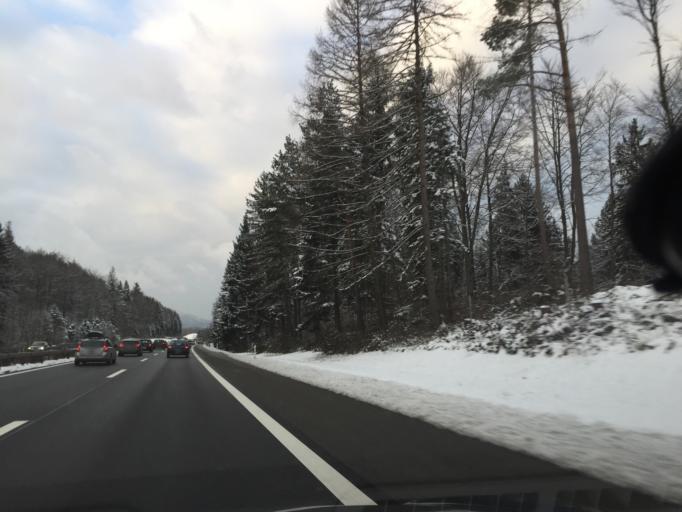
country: CH
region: Zurich
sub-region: Bezirk Horgen
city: Oberrieden / Berg
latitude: 47.2775
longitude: 8.5642
